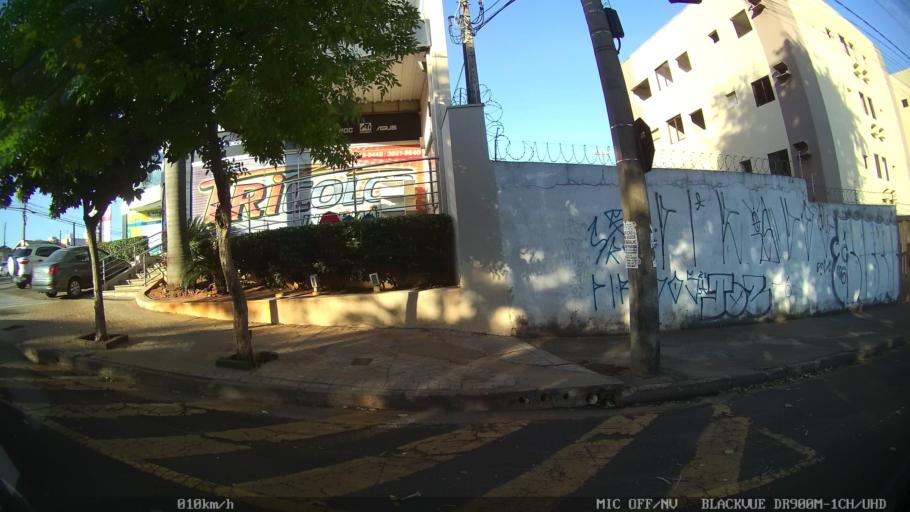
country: BR
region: Sao Paulo
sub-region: Sao Jose Do Rio Preto
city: Sao Jose do Rio Preto
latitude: -20.7955
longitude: -49.3576
